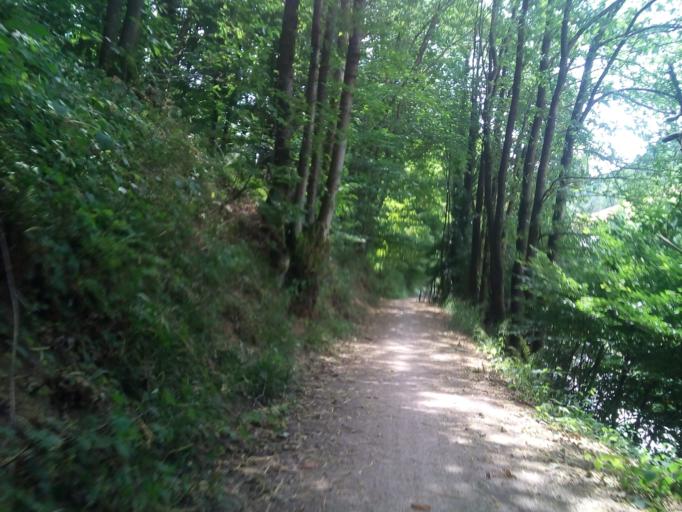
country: DE
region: Baden-Wuerttemberg
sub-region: Freiburg Region
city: Ottenhofen im Schwarzwald
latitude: 48.5722
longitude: 8.1410
